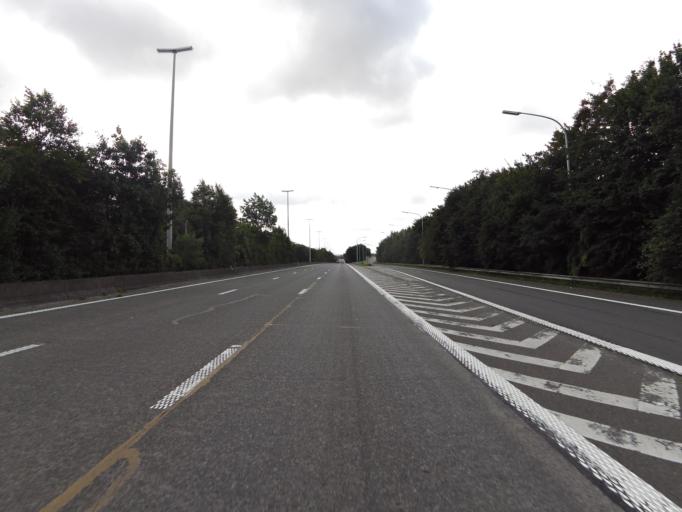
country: BE
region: Flanders
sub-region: Provincie Vlaams-Brabant
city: Tienen
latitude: 50.7449
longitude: 4.9605
